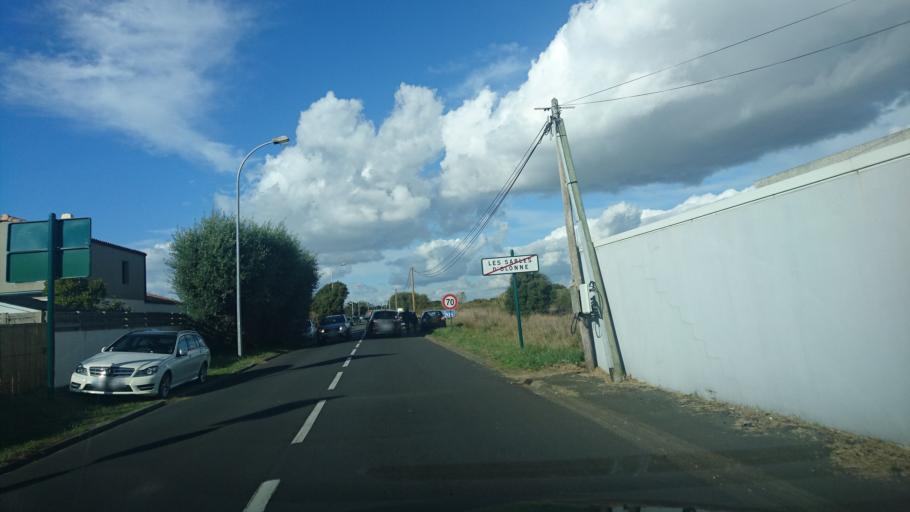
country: FR
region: Pays de la Loire
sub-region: Departement de la Vendee
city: Les Sables-d'Olonne
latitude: 46.5093
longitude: -1.8029
